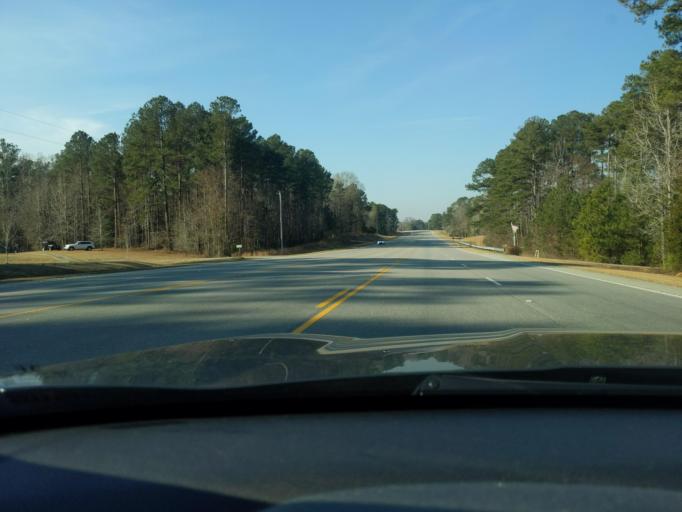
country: US
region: South Carolina
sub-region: Abbeville County
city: Abbeville
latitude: 34.1217
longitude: -82.4510
